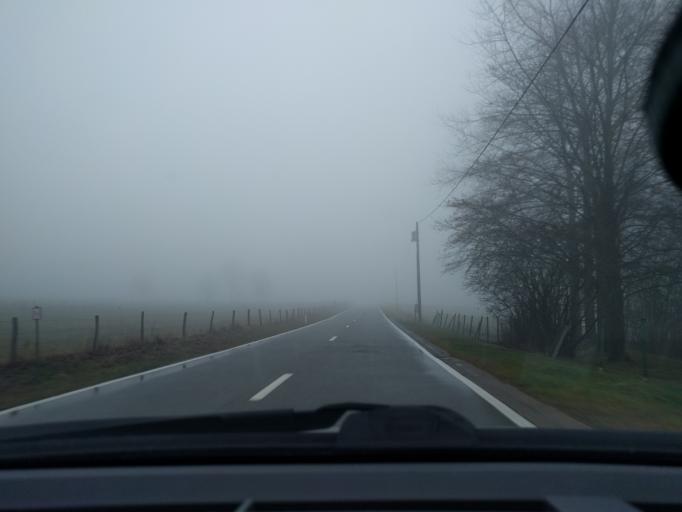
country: BE
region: Wallonia
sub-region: Province du Luxembourg
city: Gouvy
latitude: 50.1987
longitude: 5.9638
